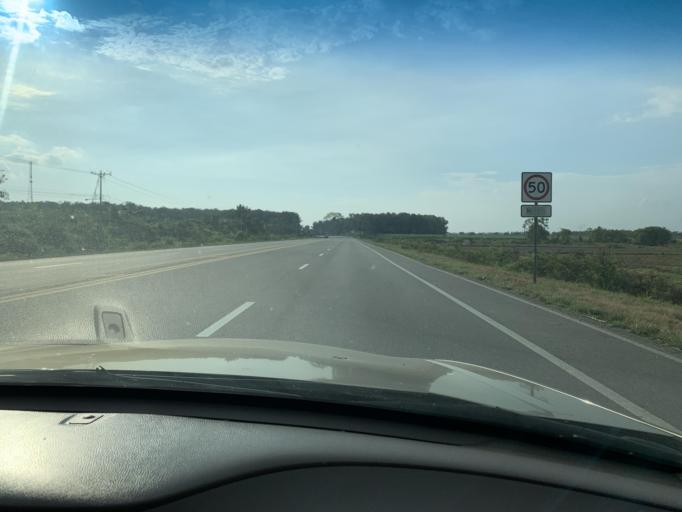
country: EC
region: Guayas
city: Coronel Marcelino Mariduena
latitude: -2.2831
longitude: -79.5164
